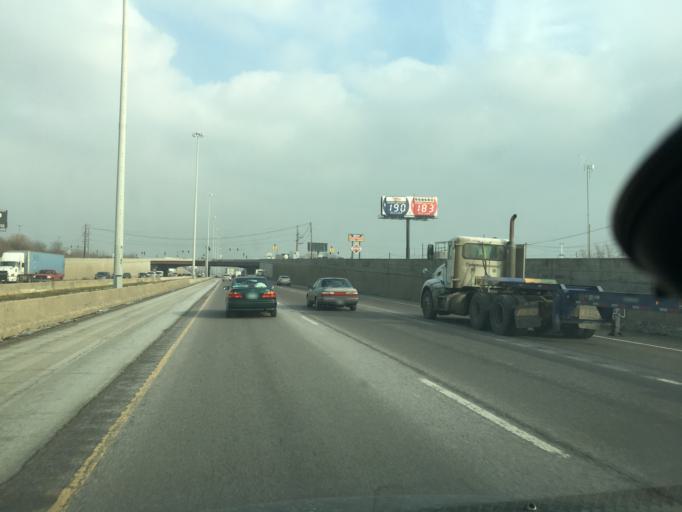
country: US
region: Illinois
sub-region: Cook County
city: Stickney
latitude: 41.8095
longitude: -87.7668
